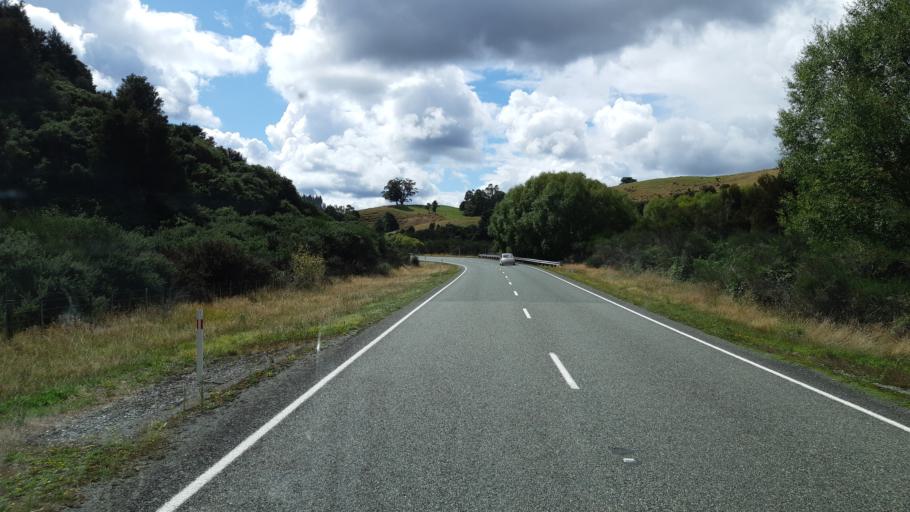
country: NZ
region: Tasman
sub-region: Tasman District
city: Wakefield
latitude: -41.6458
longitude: 172.6563
